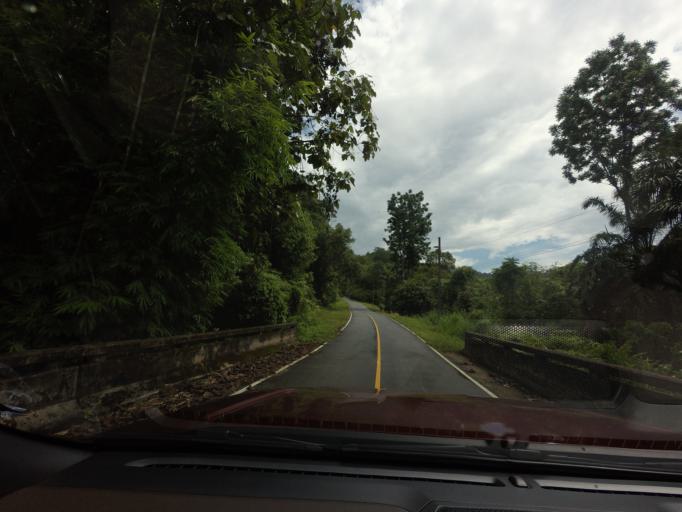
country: TH
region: Narathiwat
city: Sukhirin
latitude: 5.9289
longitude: 101.6500
